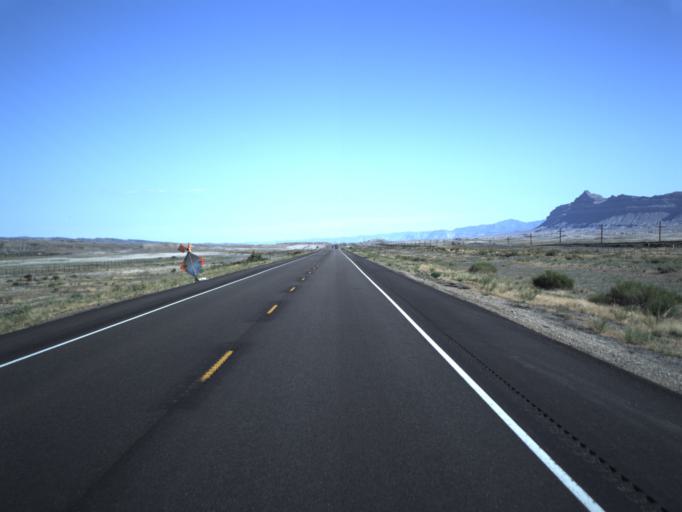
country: US
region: Utah
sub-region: Carbon County
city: East Carbon City
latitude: 39.0569
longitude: -110.3118
